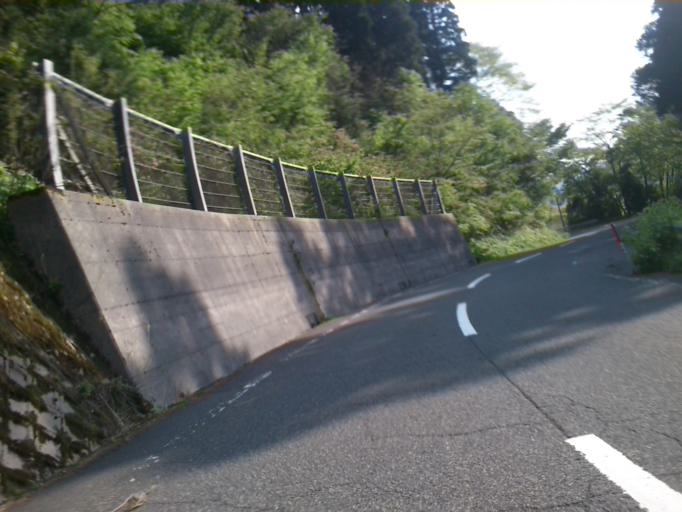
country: JP
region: Kyoto
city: Miyazu
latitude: 35.6988
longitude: 135.1782
